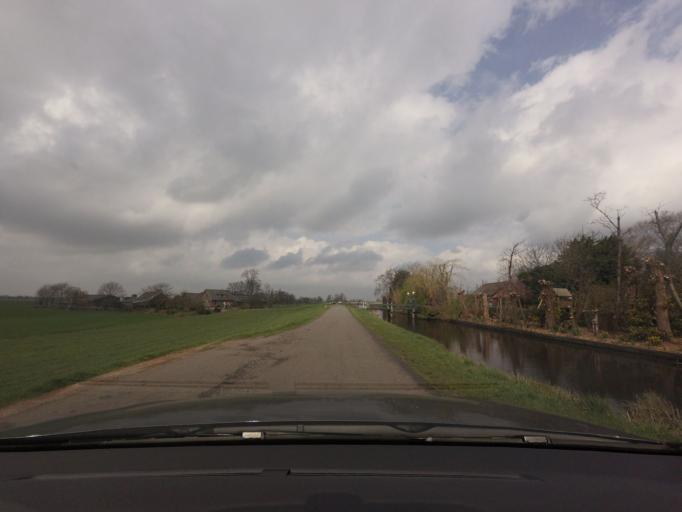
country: NL
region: North Holland
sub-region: Gemeente Uithoorn
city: Uithoorn
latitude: 52.1915
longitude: 4.8161
